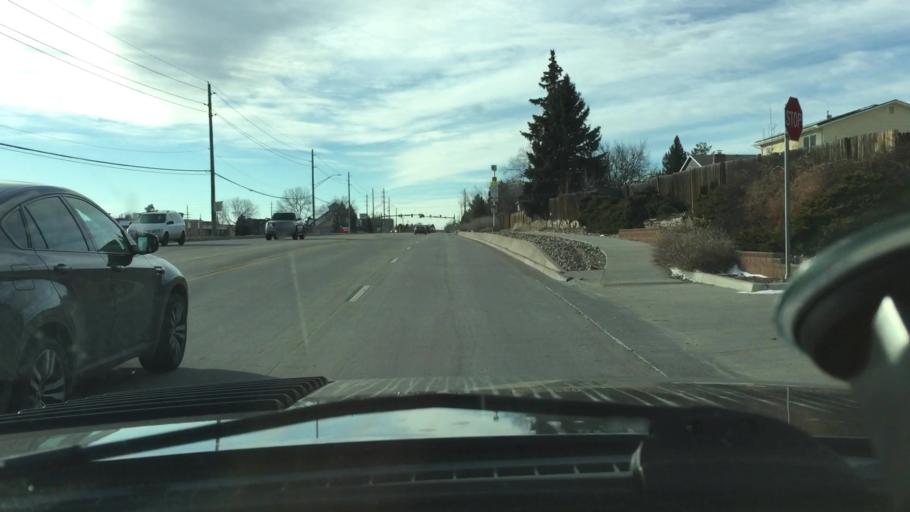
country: US
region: Colorado
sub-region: Adams County
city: Northglenn
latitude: 39.8960
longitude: -104.9968
